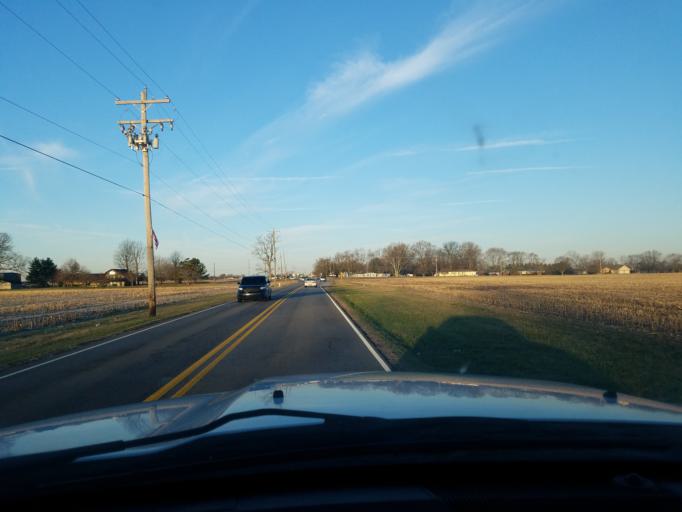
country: US
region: Indiana
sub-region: Johnson County
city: Whiteland
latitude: 39.5505
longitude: -86.0557
